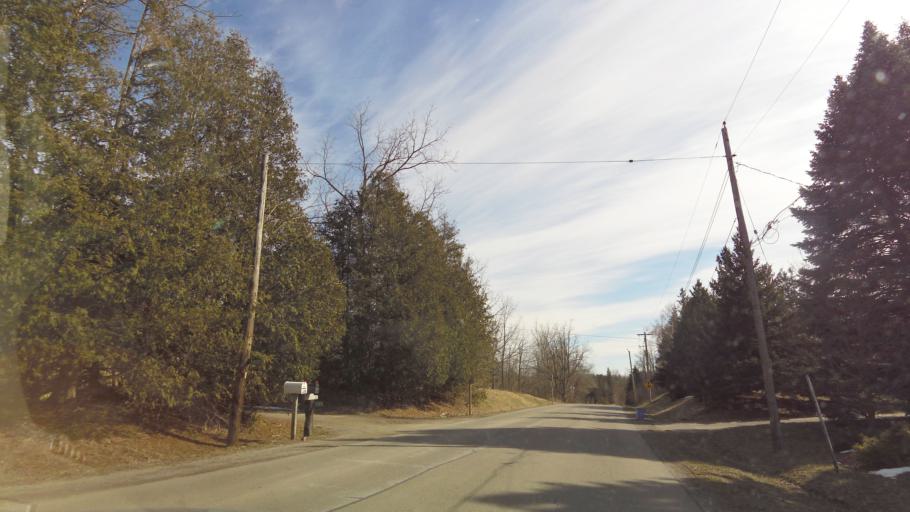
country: CA
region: Ontario
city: Burlington
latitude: 43.3995
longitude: -79.9615
